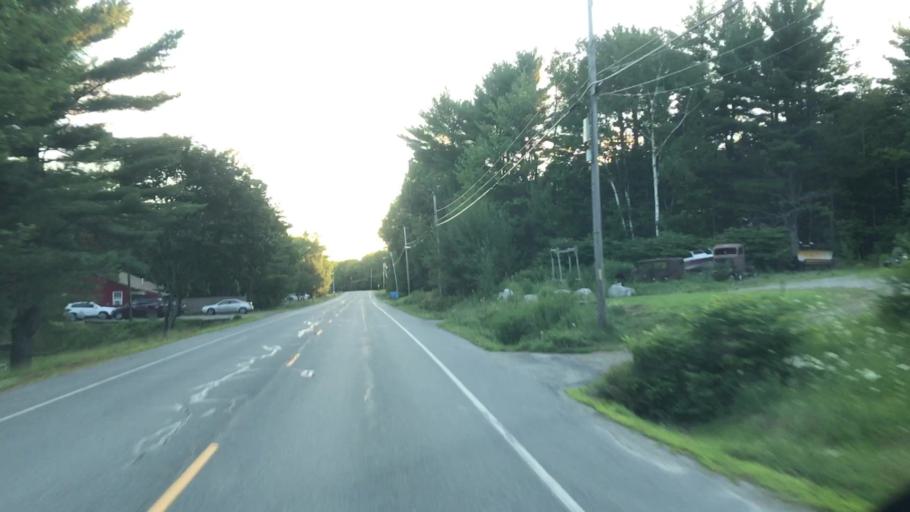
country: US
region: Maine
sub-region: Penobscot County
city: Lincoln
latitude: 45.3746
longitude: -68.4802
